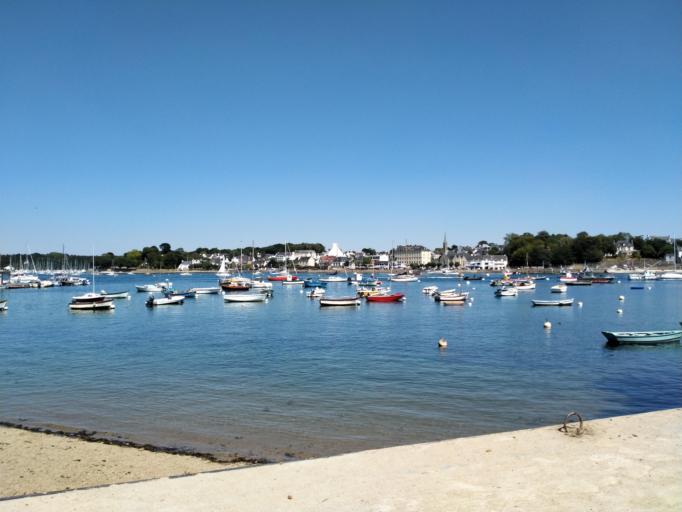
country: FR
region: Brittany
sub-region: Departement du Finistere
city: Benodet
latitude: 47.8740
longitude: -4.1205
